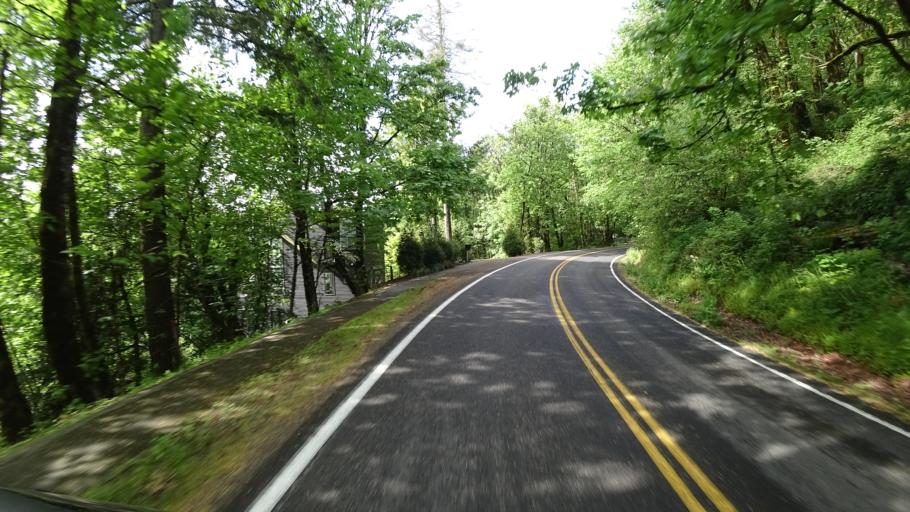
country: US
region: Oregon
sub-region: Washington County
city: West Haven
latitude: 45.5346
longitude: -122.7580
